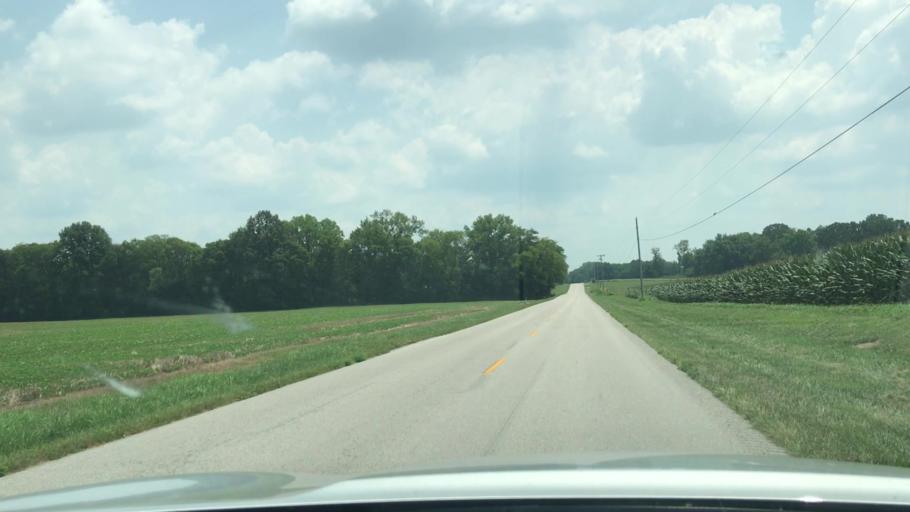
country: US
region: Kentucky
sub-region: Todd County
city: Elkton
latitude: 36.7664
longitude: -87.1105
